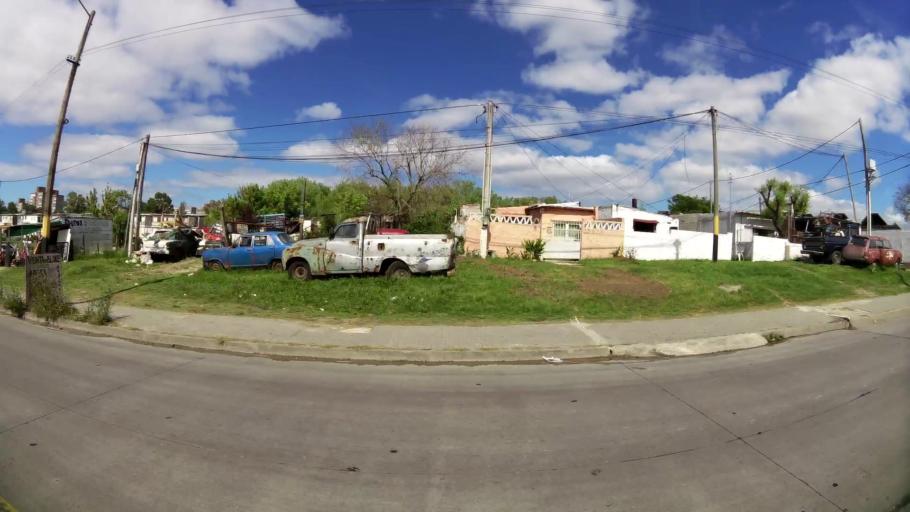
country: UY
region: Canelones
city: Paso de Carrasco
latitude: -34.8777
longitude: -56.1113
